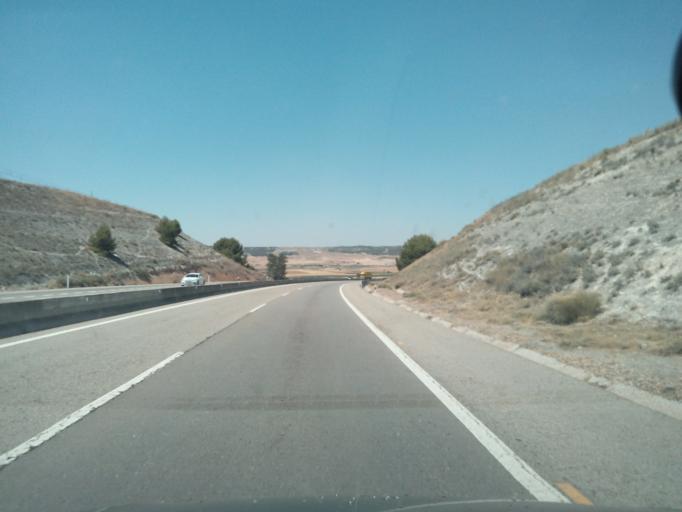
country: ES
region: Castille-La Mancha
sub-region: Province of Toledo
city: Tembleque
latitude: 39.7844
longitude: -3.4830
